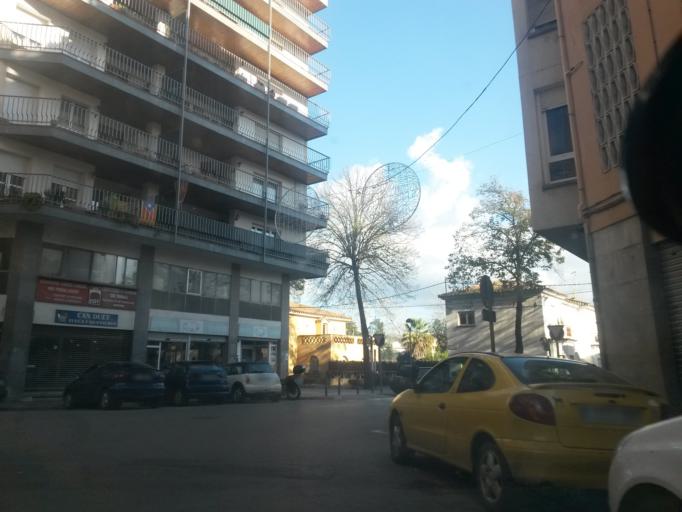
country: ES
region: Catalonia
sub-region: Provincia de Girona
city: Girona
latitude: 41.9778
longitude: 2.8134
